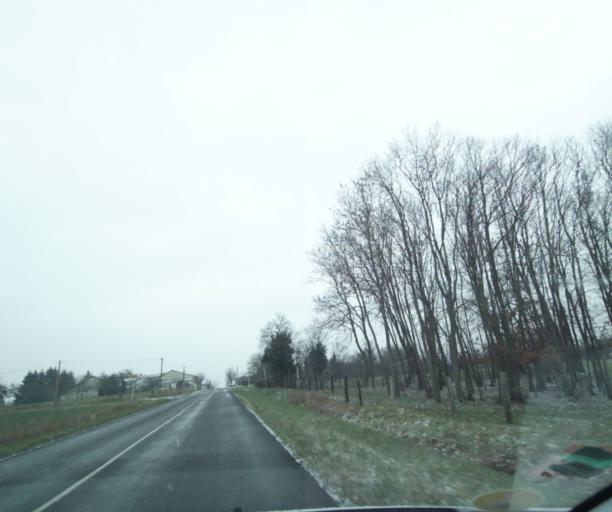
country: FR
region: Champagne-Ardenne
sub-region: Departement de la Haute-Marne
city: Wassy
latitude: 48.4627
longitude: 5.0319
